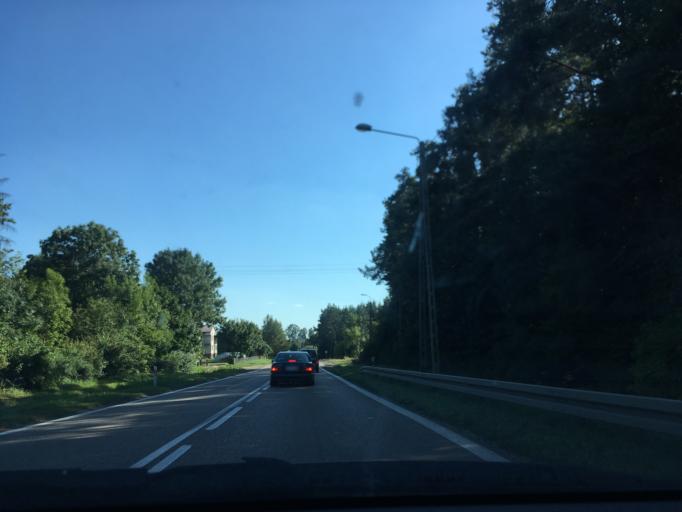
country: PL
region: Podlasie
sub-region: Powiat sokolski
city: Suchowola
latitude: 53.5528
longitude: 23.0997
